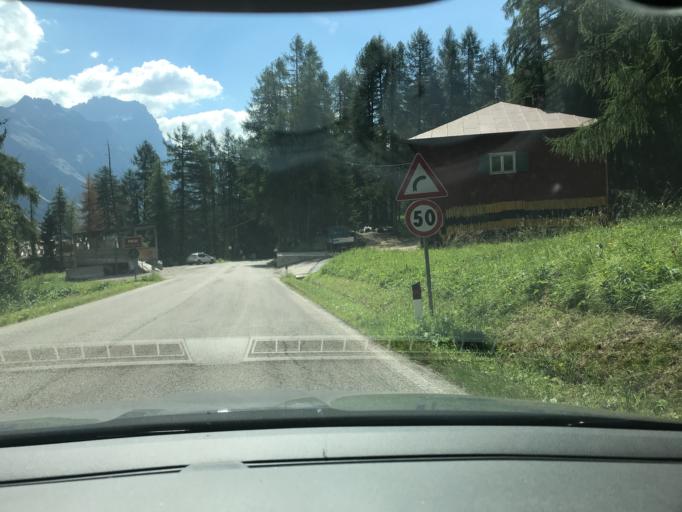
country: IT
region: Veneto
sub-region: Provincia di Belluno
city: Cortina d'Ampezzo
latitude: 46.5239
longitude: 12.1079
